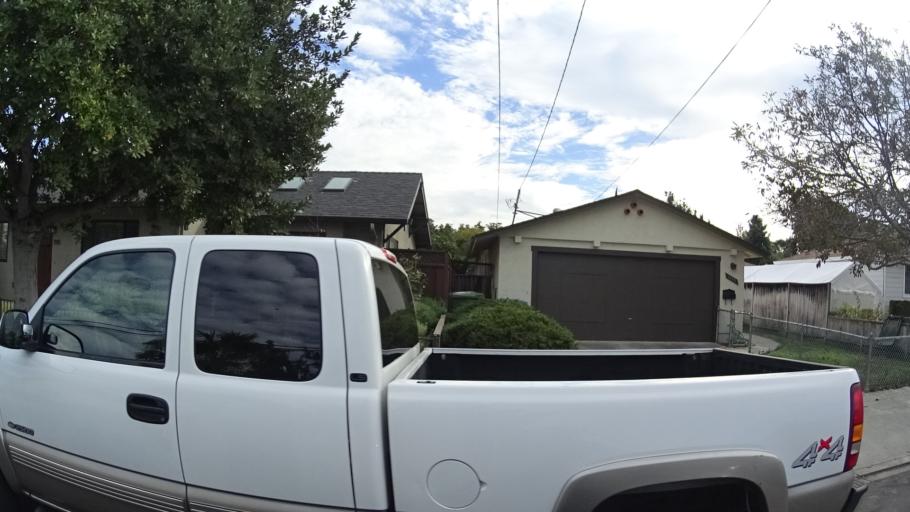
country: US
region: California
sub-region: Santa Clara County
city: Santa Clara
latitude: 37.3572
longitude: -121.9516
